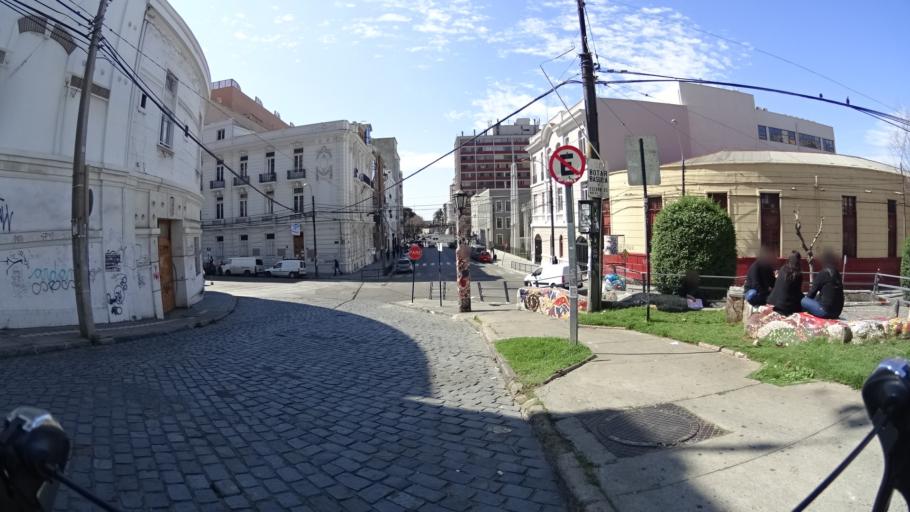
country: CL
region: Valparaiso
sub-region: Provincia de Valparaiso
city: Valparaiso
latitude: -33.0481
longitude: -71.6199
